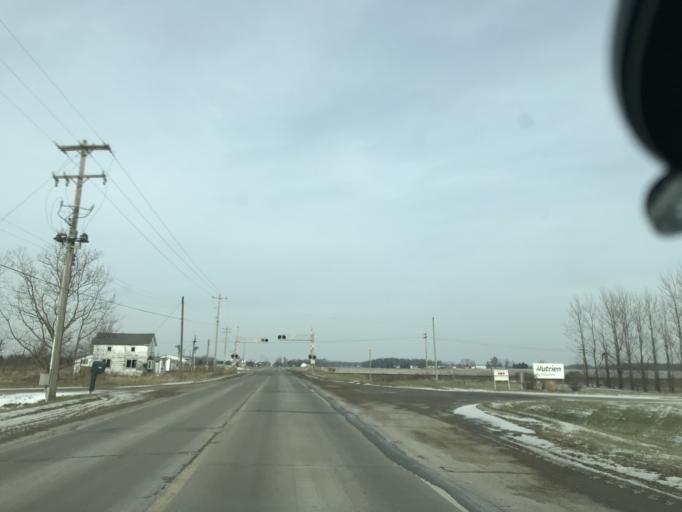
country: US
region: Michigan
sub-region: Ionia County
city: Lake Odessa
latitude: 42.7621
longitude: -85.0743
